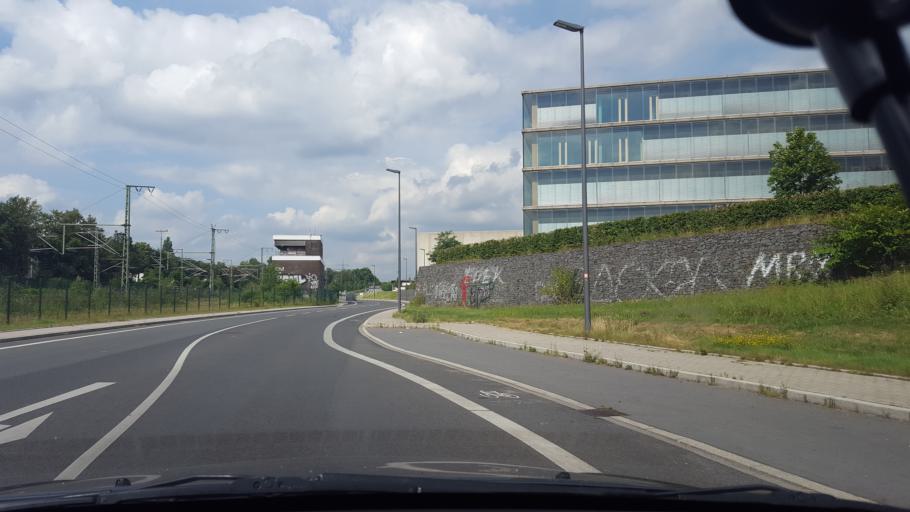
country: DE
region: North Rhine-Westphalia
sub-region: Regierungsbezirk Munster
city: Recklinghausen
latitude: 51.6210
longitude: 7.2063
